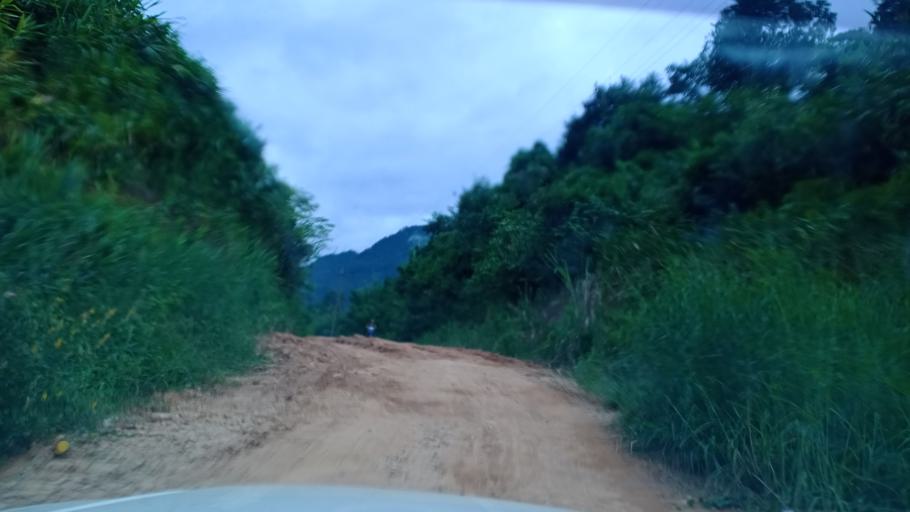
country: TH
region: Changwat Bueng Kan
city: Pak Khat
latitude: 18.7279
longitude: 103.2753
